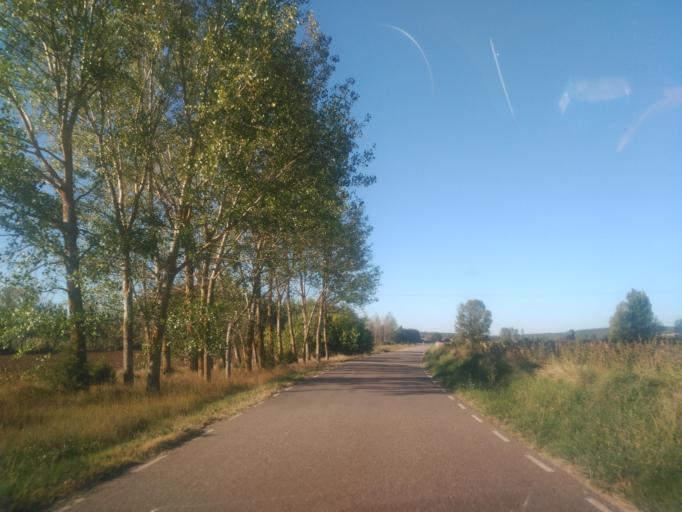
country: ES
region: Castille and Leon
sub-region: Provincia de Burgos
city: Brazacorta
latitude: 41.7139
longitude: -3.3705
